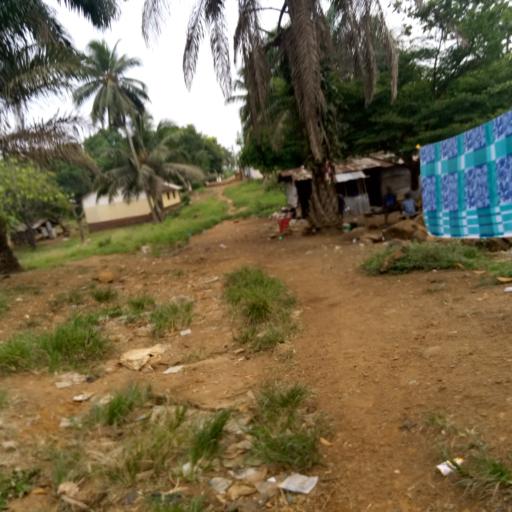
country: LR
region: Montserrado
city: Monrovia
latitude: 6.3008
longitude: -10.6869
